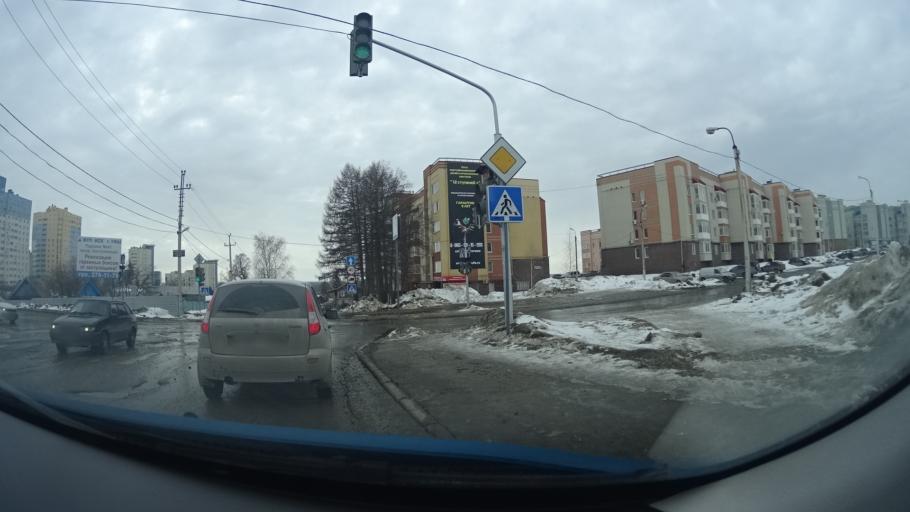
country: RU
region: Bashkortostan
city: Ufa
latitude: 54.6935
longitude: 55.9883
